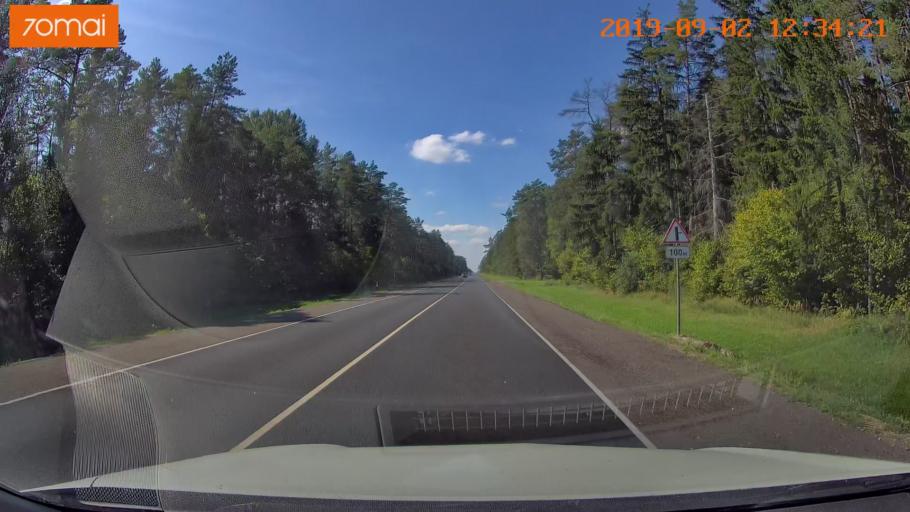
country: RU
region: Smolensk
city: Shumyachi
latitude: 53.8111
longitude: 32.4068
